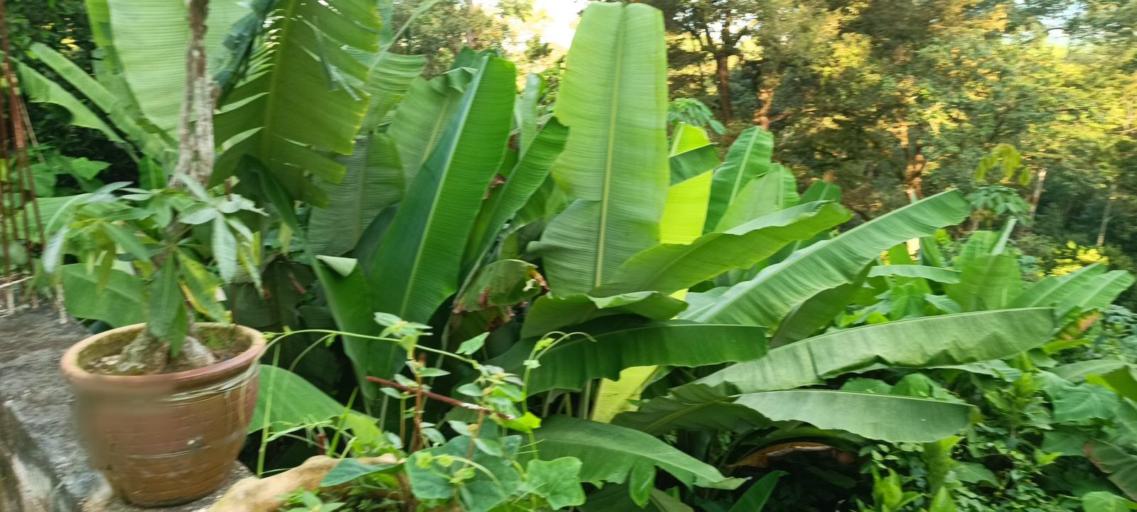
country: MY
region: Penang
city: Bukit Mertajam
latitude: 5.3732
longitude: 100.4759
